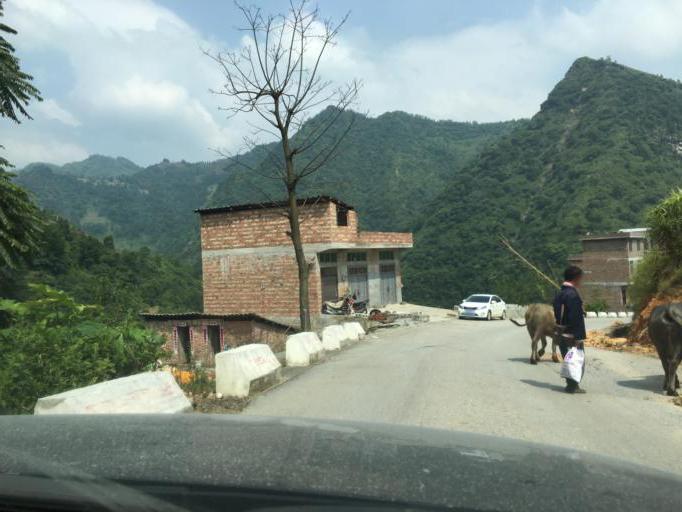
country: CN
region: Guangxi Zhuangzu Zizhiqu
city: Tongle
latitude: 25.2965
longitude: 106.2658
